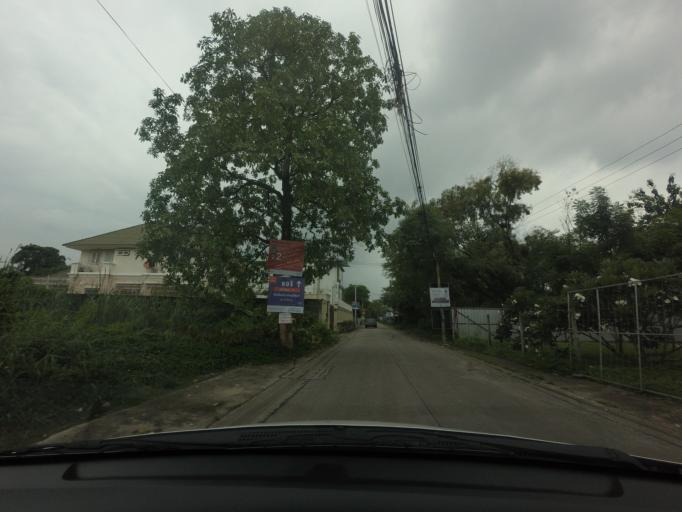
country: TH
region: Bangkok
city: Lak Si
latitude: 13.8970
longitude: 100.5698
